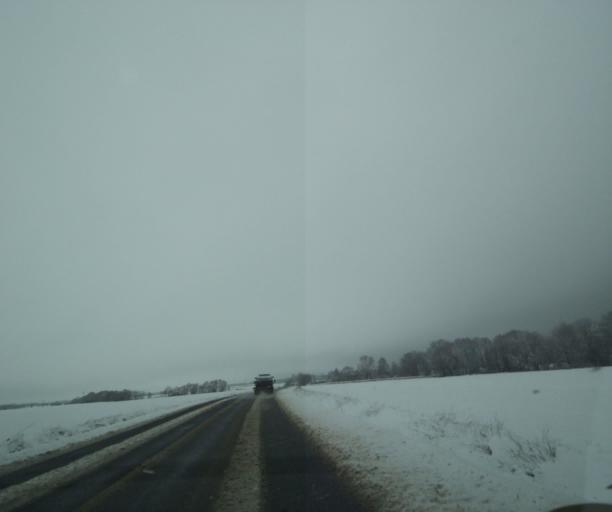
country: FR
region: Champagne-Ardenne
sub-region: Departement de la Haute-Marne
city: Saint-Dizier
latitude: 48.5667
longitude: 4.9208
